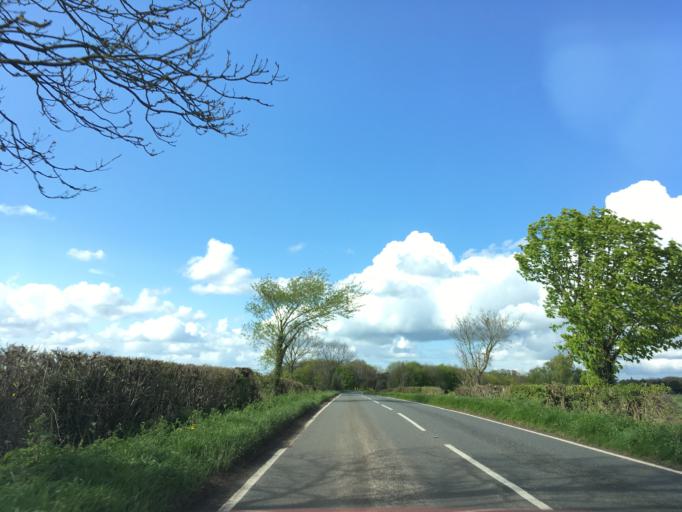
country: GB
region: England
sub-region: Gloucestershire
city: Tetbury
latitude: 51.6629
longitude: -2.1785
